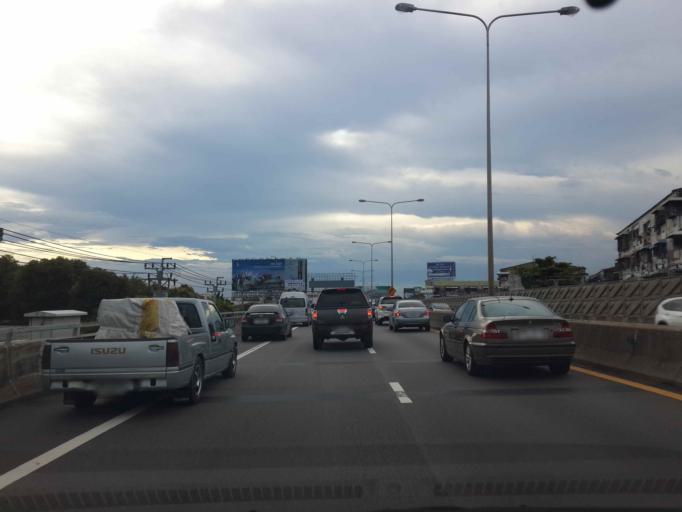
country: TH
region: Bangkok
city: Rat Burana
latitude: 13.6708
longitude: 100.4972
